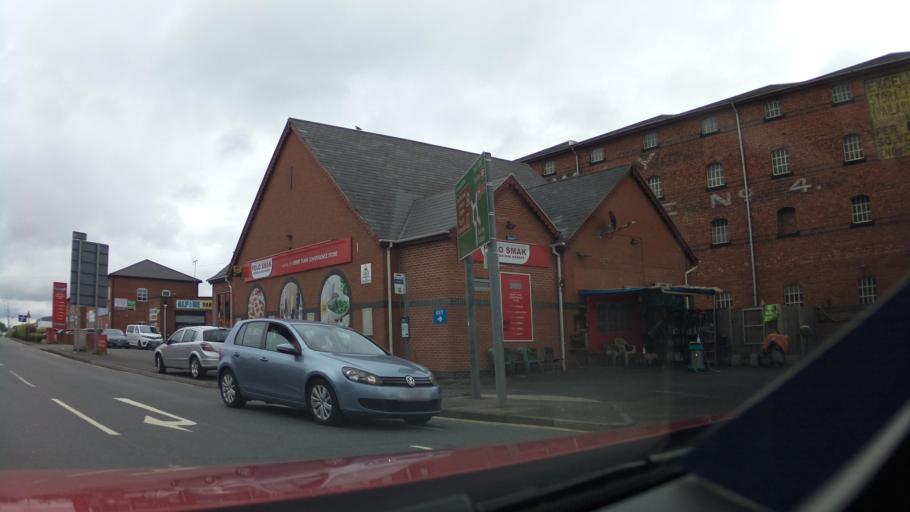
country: GB
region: England
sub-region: Staffordshire
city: Burton upon Trent
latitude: 52.8139
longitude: -1.6353
